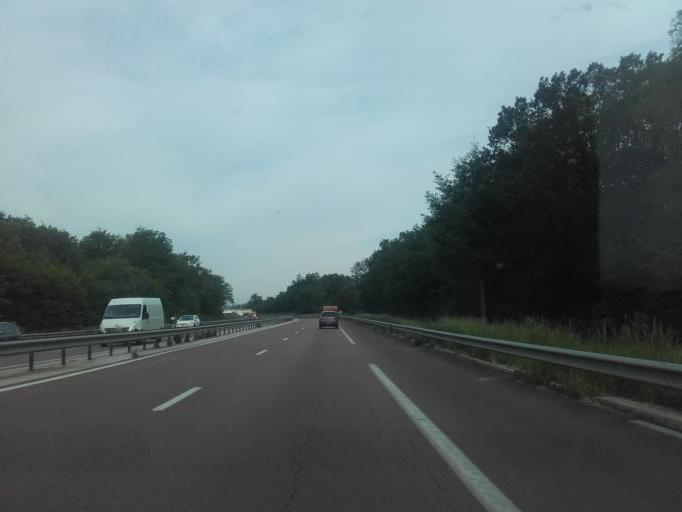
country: FR
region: Bourgogne
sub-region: Departement de Saone-et-Loire
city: Givry
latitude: 46.7602
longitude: 4.7510
